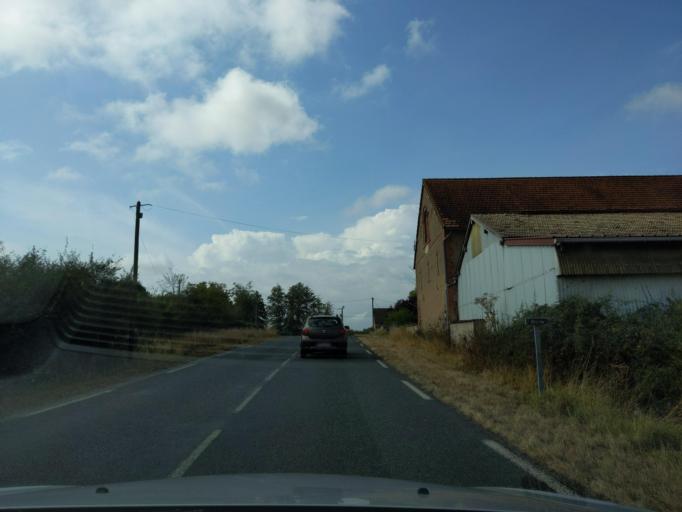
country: FR
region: Bourgogne
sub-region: Departement de Saone-et-Loire
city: Bourbon-Lancy
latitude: 46.6649
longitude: 3.8017
